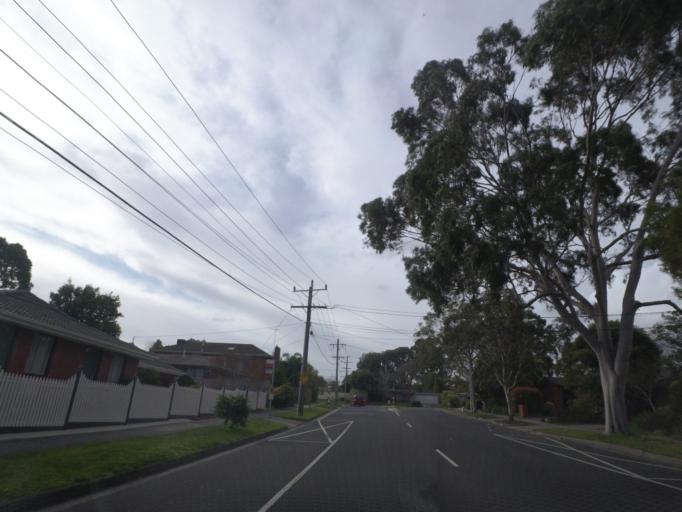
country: AU
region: Victoria
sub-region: Whitehorse
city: Vermont South
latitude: -37.8611
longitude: 145.1828
